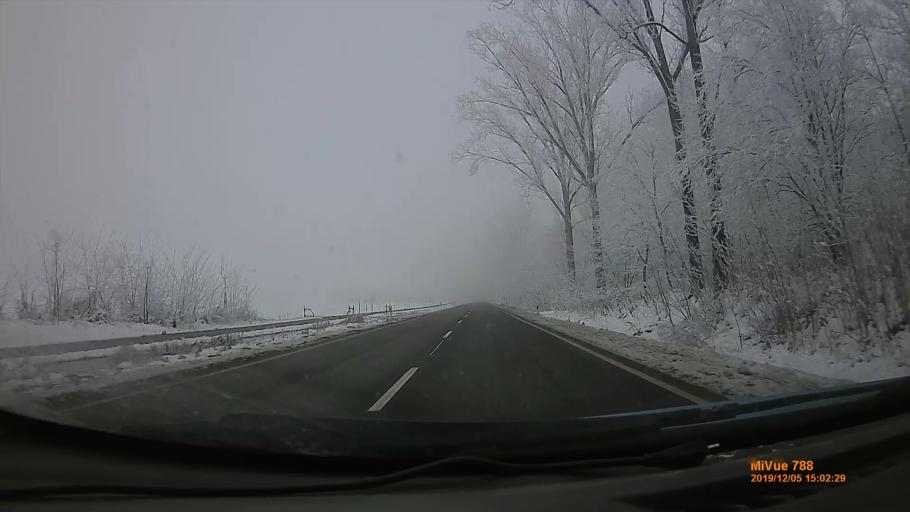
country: HU
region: Szabolcs-Szatmar-Bereg
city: Tiszanagyfalu
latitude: 48.0763
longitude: 21.5135
